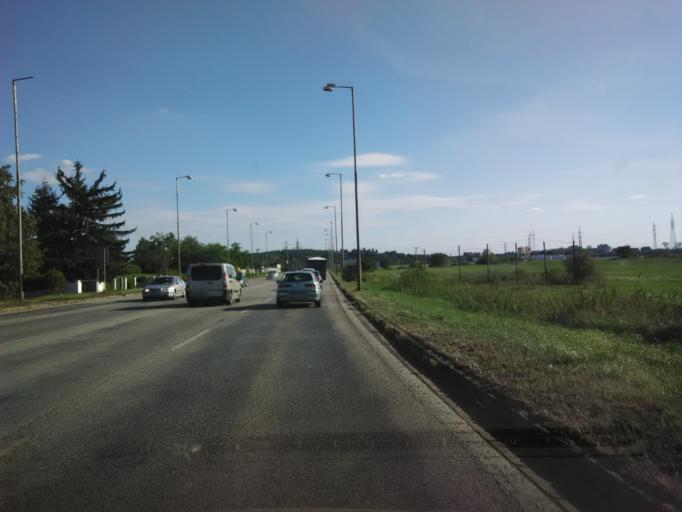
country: SK
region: Nitriansky
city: Levice
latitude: 48.2380
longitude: 18.5965
